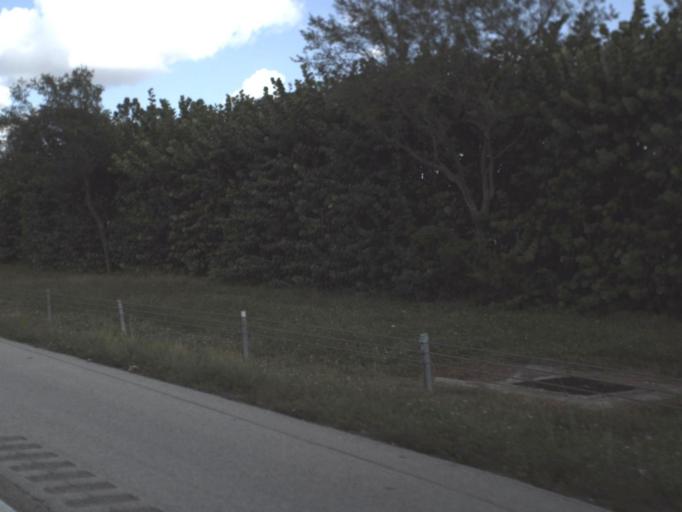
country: US
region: Florida
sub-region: Palm Beach County
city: Boca Pointe
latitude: 26.3441
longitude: -80.1703
